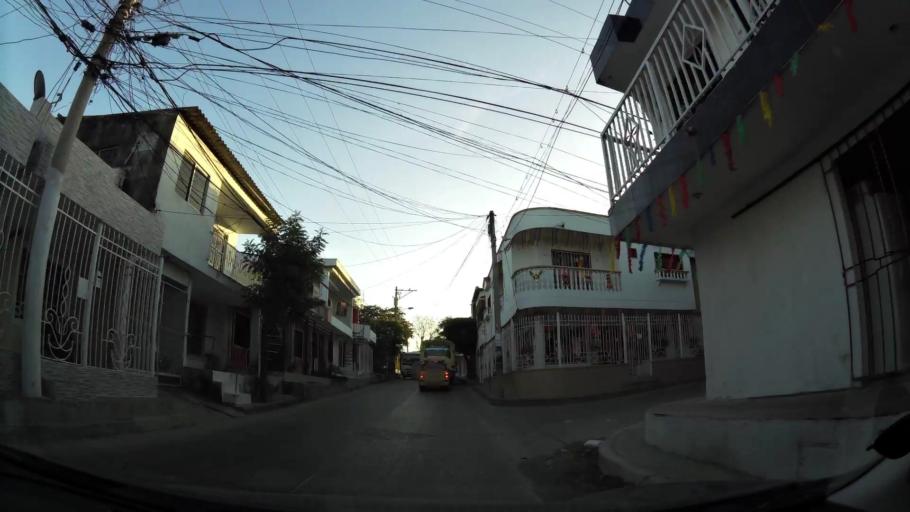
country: CO
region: Atlantico
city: Soledad
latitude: 10.9220
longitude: -74.7955
